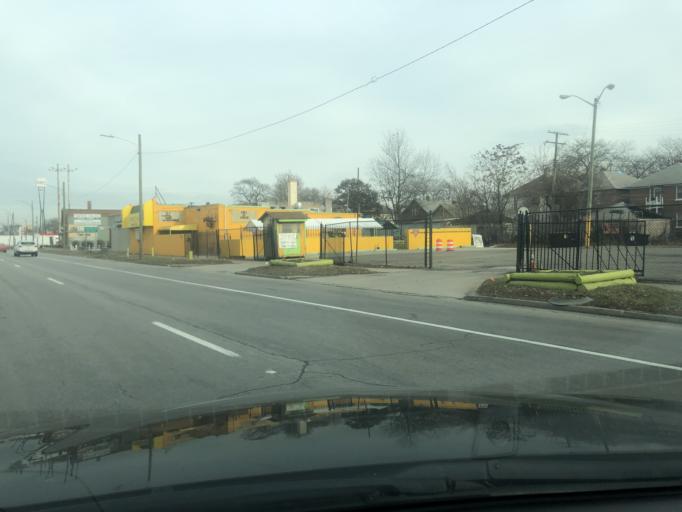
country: US
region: Michigan
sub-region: Wayne County
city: Melvindale
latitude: 42.2747
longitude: -83.1564
